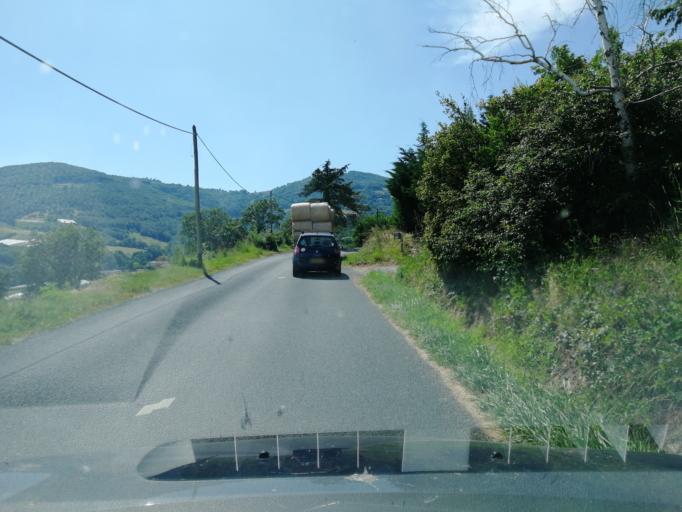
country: FR
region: Rhone-Alpes
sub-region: Departement du Rhone
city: Saint-Didier-sous-Riverie
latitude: 45.6326
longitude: 4.6312
